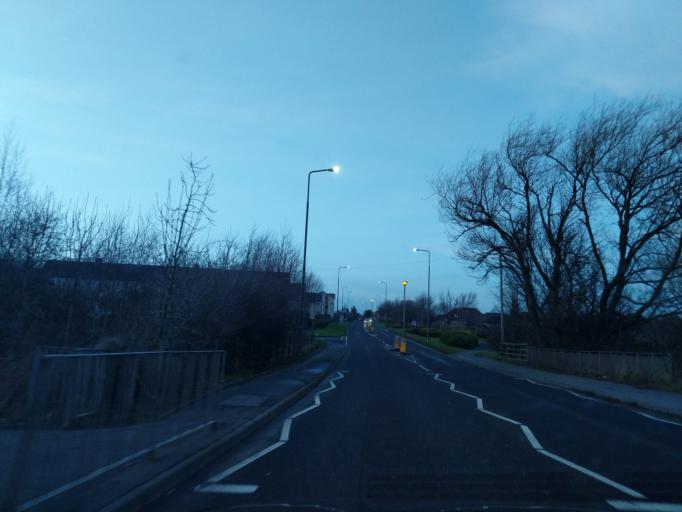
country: GB
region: Scotland
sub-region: Midlothian
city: Bonnyrigg
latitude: 55.8698
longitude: -3.0934
